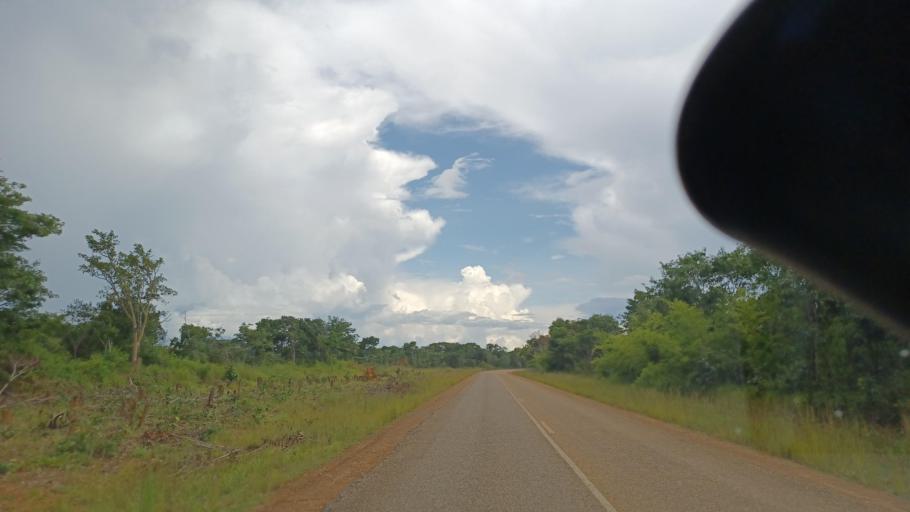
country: ZM
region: North-Western
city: Kasempa
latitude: -13.1295
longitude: 25.8751
